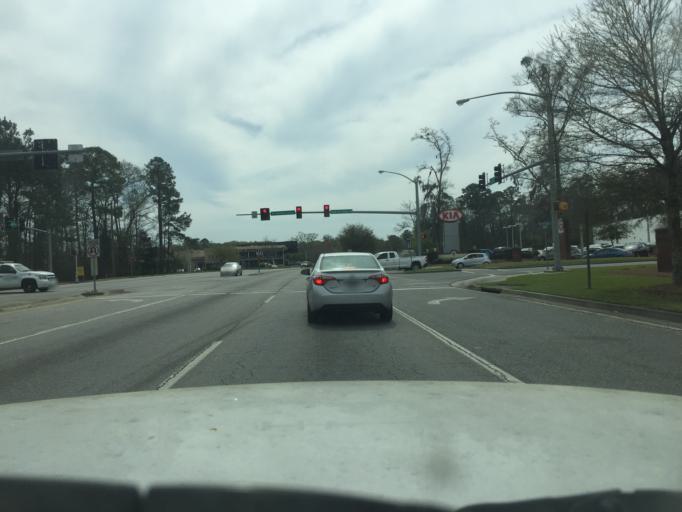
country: US
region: Georgia
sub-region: Chatham County
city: Garden City
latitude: 32.0662
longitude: -81.1602
